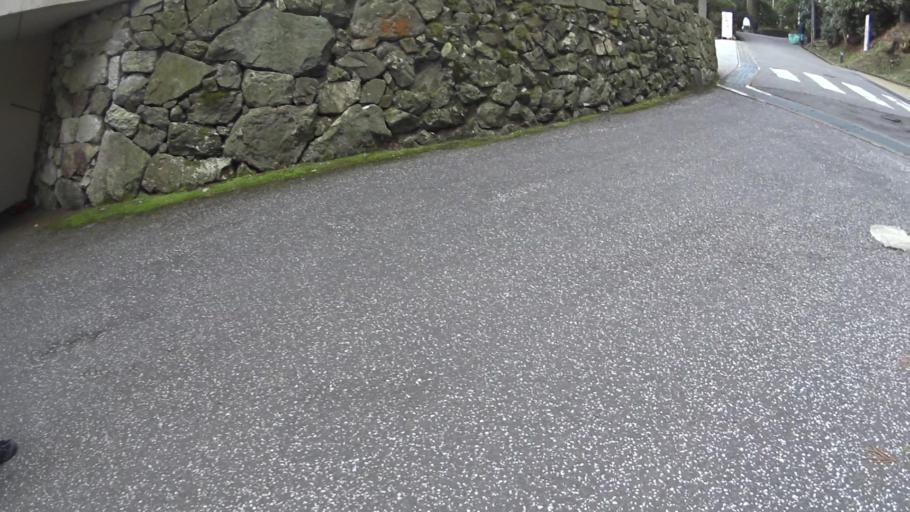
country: JP
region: Shiga Prefecture
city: Otsu-shi
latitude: 35.0684
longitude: 135.8418
